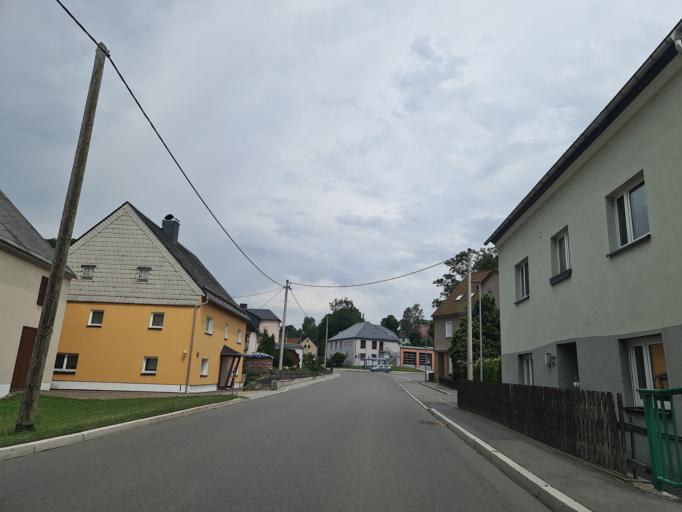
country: DE
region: Saxony
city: Pfaffroda
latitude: 50.6978
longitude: 13.3521
